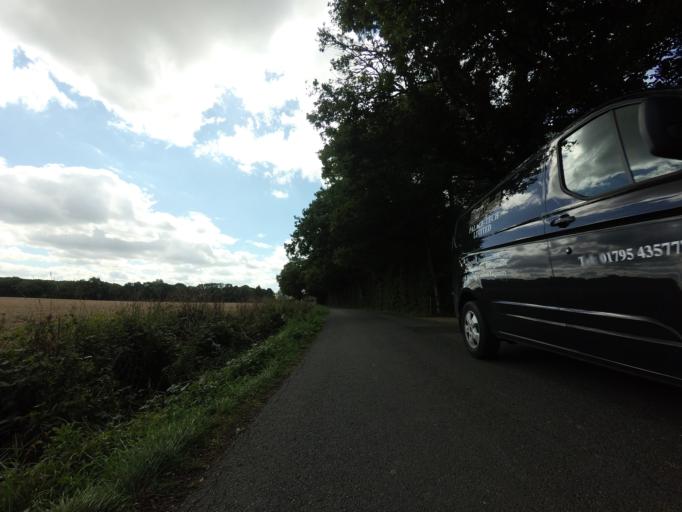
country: GB
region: England
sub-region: Kent
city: Marden
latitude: 51.1510
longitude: 0.5153
